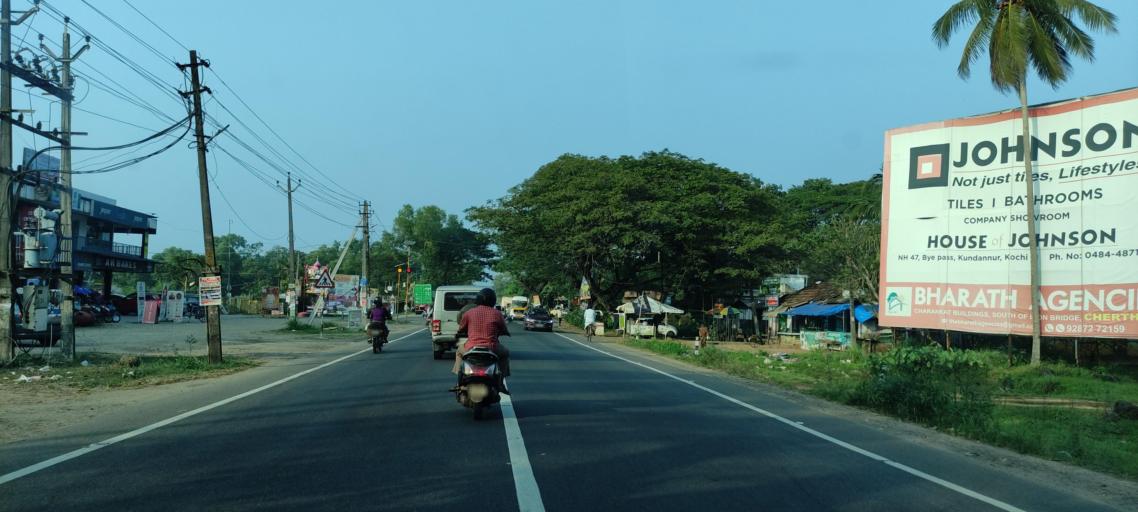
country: IN
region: Kerala
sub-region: Alappuzha
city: Shertallai
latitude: 9.6273
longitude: 76.3328
